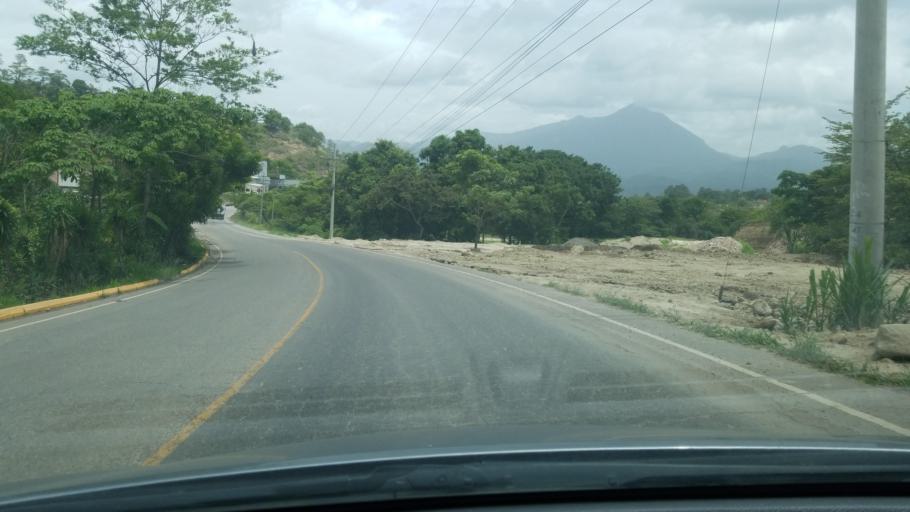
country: HN
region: Copan
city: Cucuyagua
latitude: 14.6705
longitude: -88.8554
